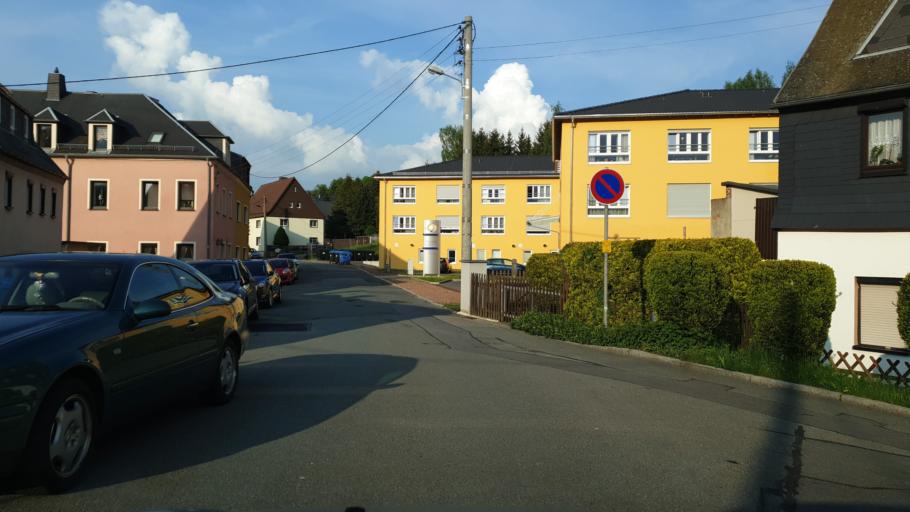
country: DE
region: Saxony
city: Stollberg
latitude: 50.7117
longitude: 12.7842
